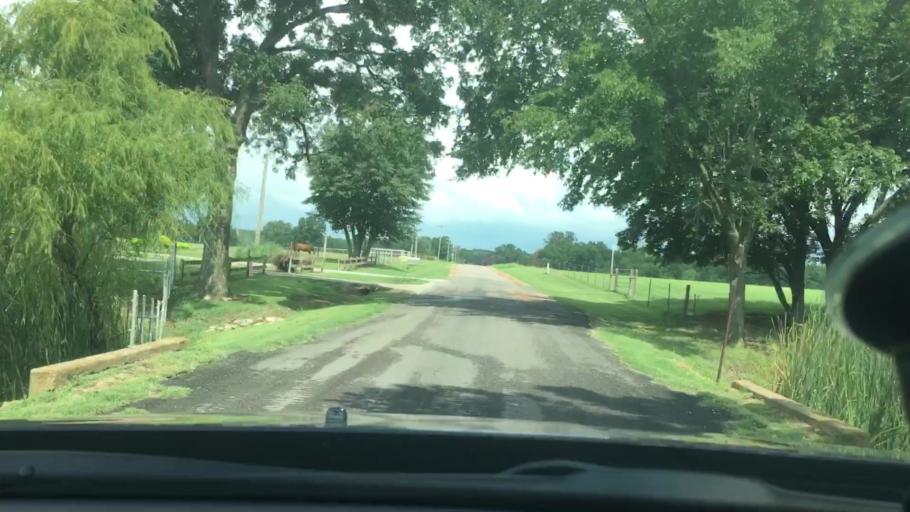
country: US
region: Oklahoma
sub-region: Carter County
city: Dickson
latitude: 34.2348
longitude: -96.9157
